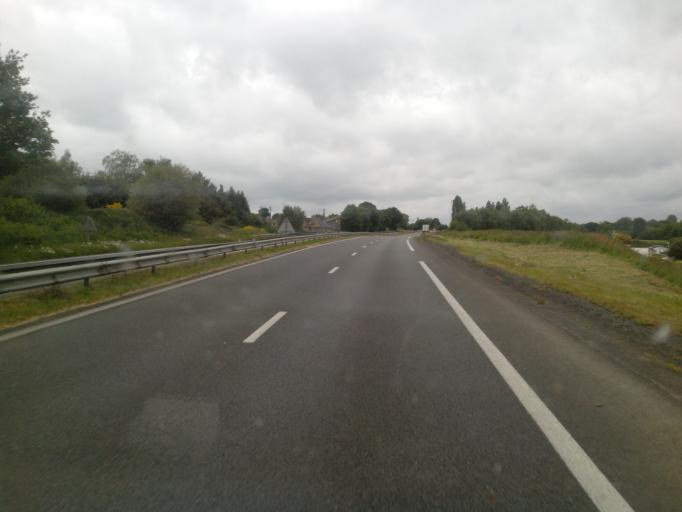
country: FR
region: Brittany
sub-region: Departement des Cotes-d'Armor
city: Graces
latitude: 48.5652
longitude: -3.2031
